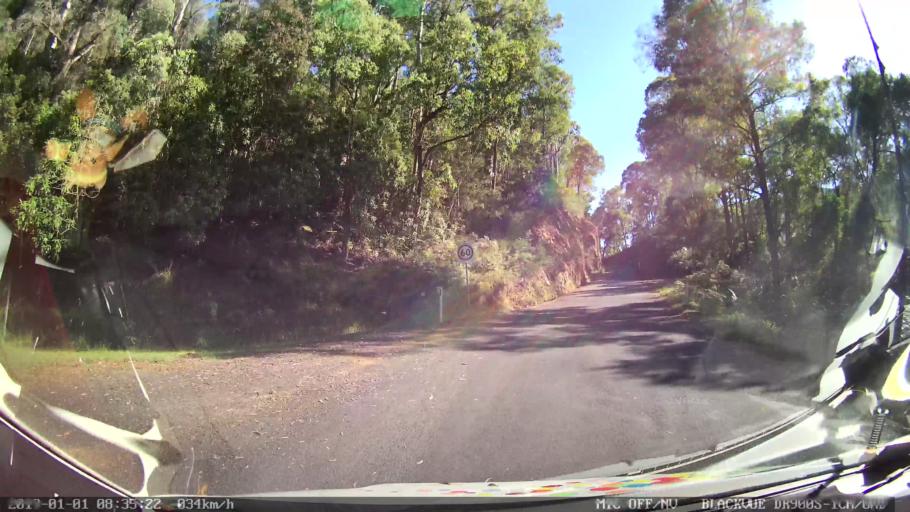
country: AU
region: New South Wales
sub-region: Snowy River
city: Jindabyne
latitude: -36.3494
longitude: 148.1934
